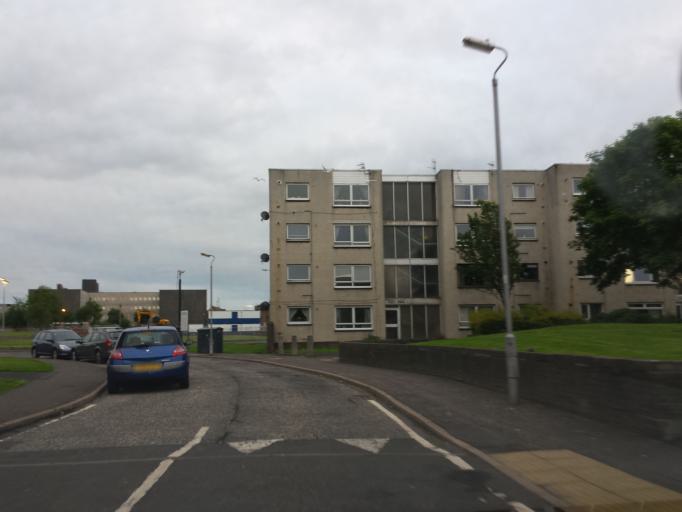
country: GB
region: Scotland
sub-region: South Ayrshire
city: Ayr
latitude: 55.4686
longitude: -4.6254
